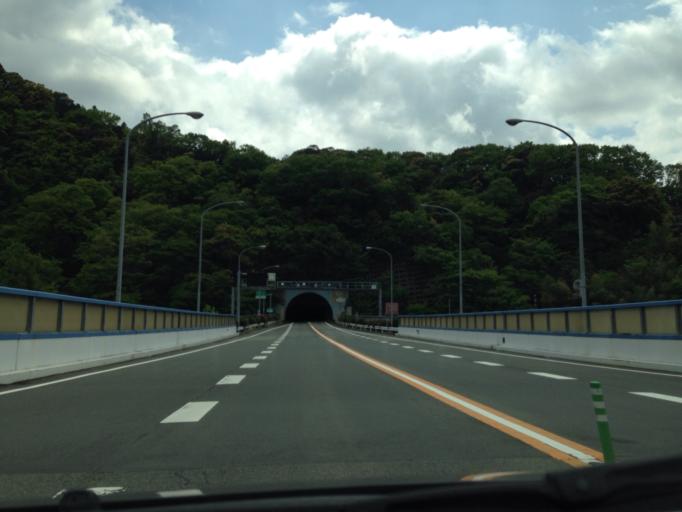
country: JP
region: Shizuoka
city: Mishima
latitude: 34.9897
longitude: 138.9343
